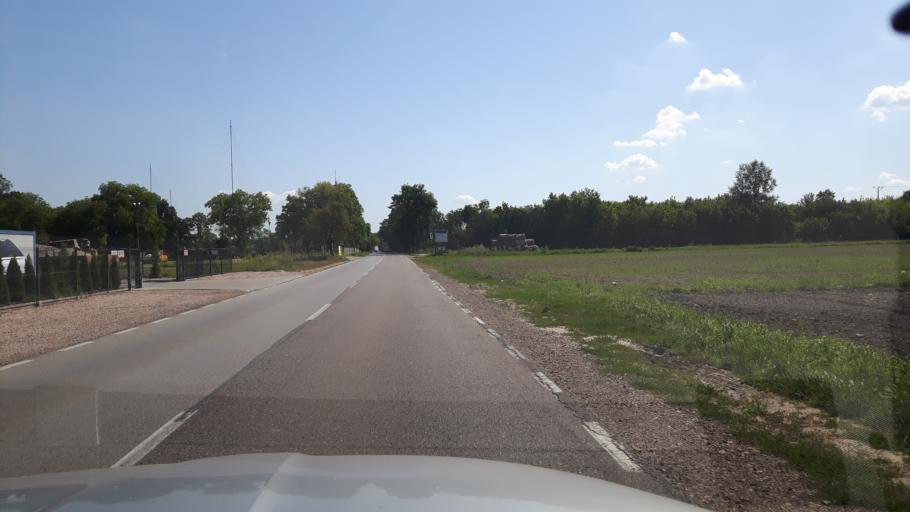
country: PL
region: Masovian Voivodeship
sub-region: Powiat pruszkowski
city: Nowe Grocholice
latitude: 52.1426
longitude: 20.8962
